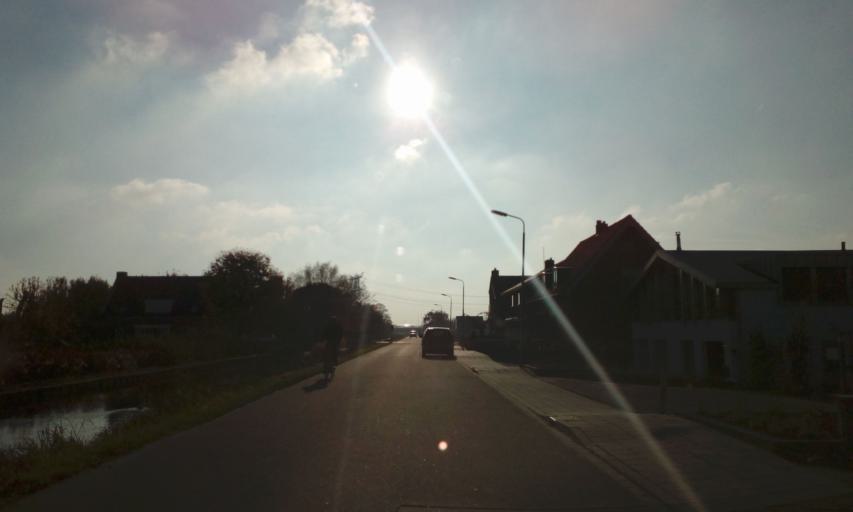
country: NL
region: South Holland
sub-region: Gemeente Lansingerland
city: Bleiswijk
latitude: 52.0426
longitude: 4.5448
